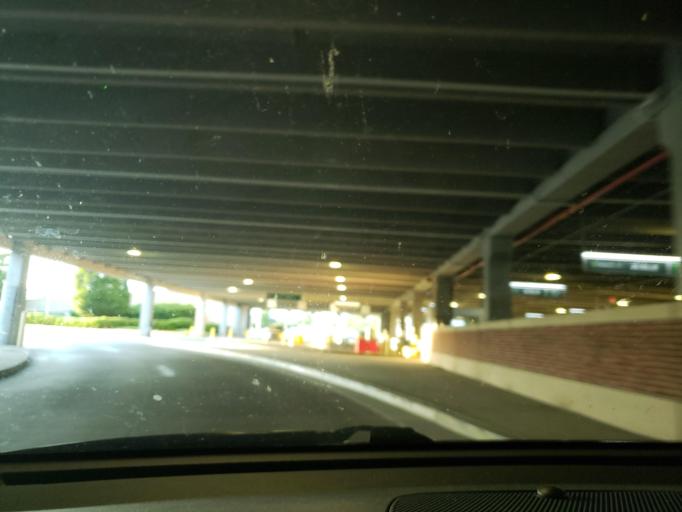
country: US
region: Virginia
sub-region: Henrico County
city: Fort Lee
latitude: 37.5098
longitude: -77.3330
